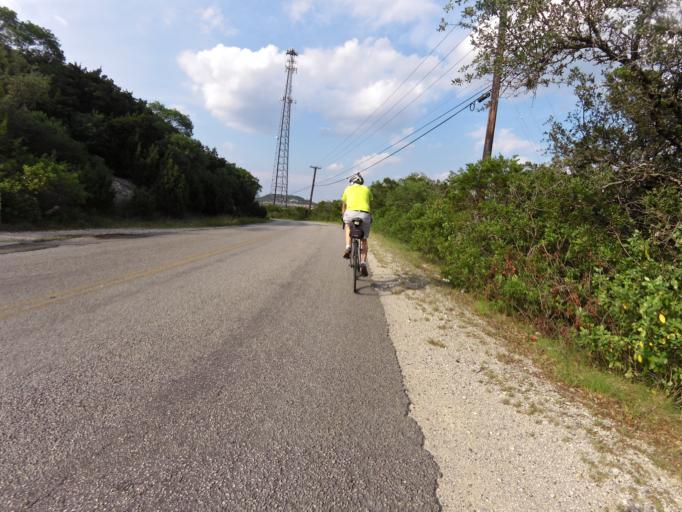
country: US
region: Texas
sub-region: Bexar County
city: Cross Mountain
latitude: 29.6586
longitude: -98.6309
